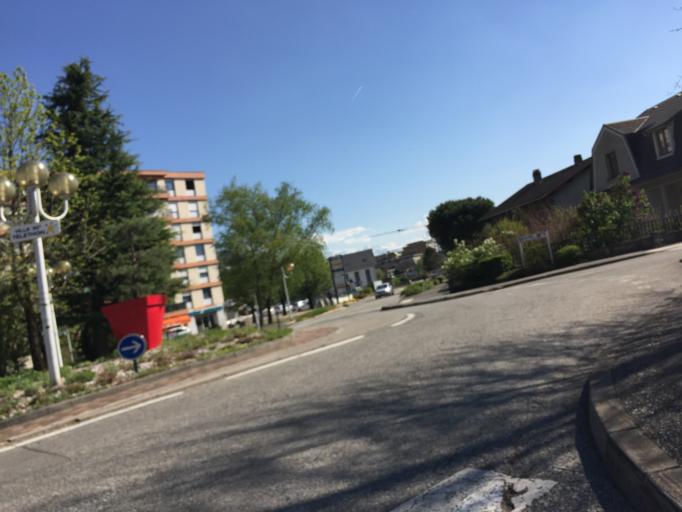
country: FR
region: Rhone-Alpes
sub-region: Departement de la Savoie
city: Barby
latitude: 45.5723
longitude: 5.9771
